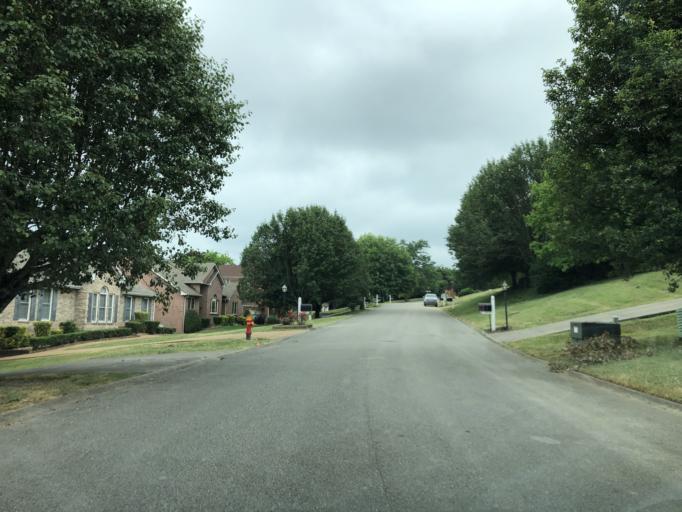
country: US
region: Tennessee
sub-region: Davidson County
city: Goodlettsville
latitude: 36.2940
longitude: -86.7377
